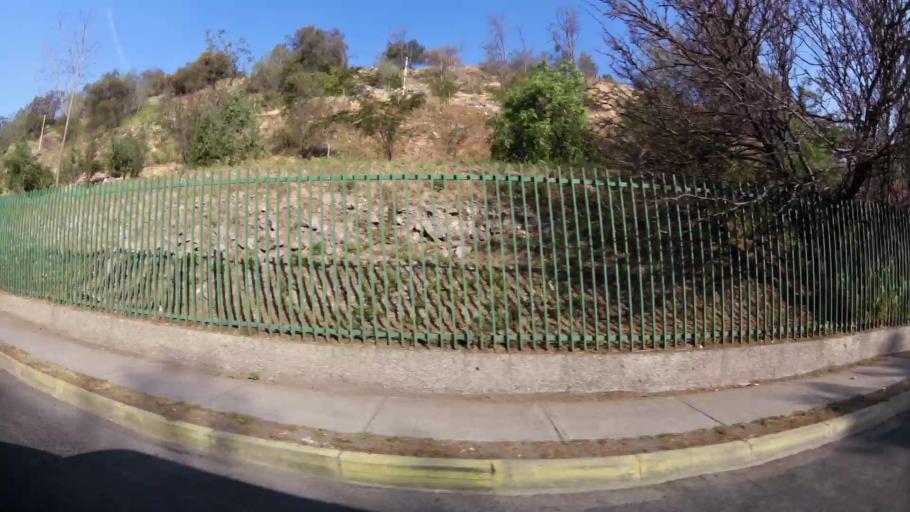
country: CL
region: Santiago Metropolitan
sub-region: Provincia de Santiago
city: Santiago
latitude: -33.4175
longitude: -70.6470
